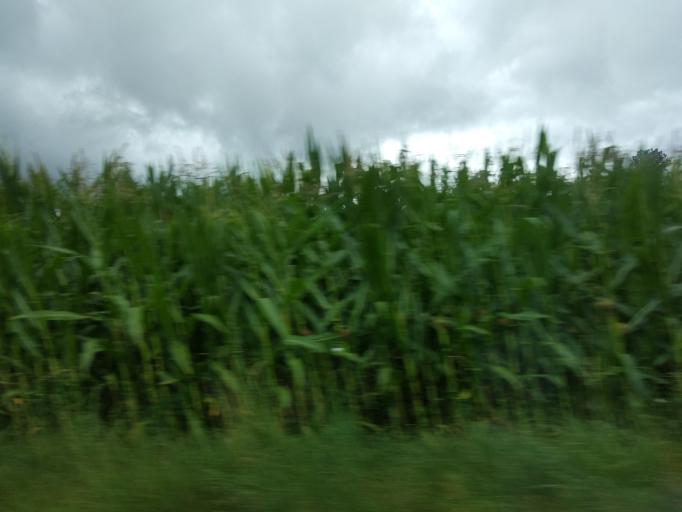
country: DE
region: Bavaria
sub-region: Swabia
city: Benningen
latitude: 47.9704
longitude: 10.2365
